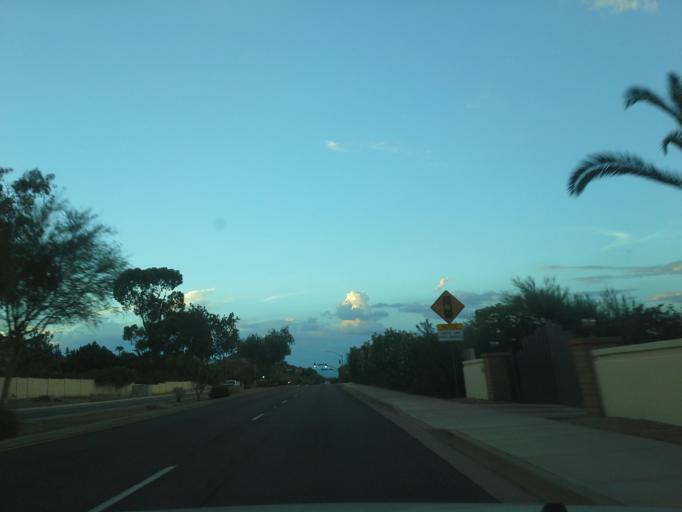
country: US
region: Arizona
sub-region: Maricopa County
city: Paradise Valley
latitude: 33.5512
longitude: -111.9756
